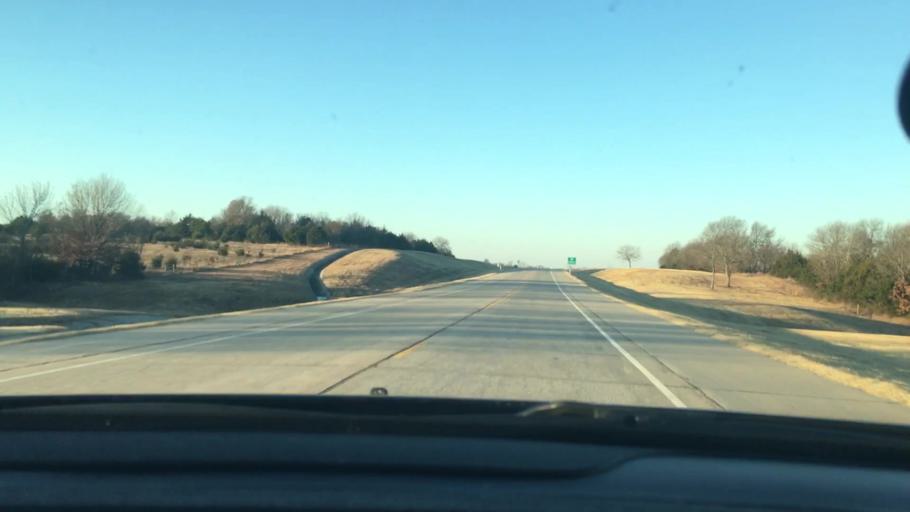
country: US
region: Oklahoma
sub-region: Murray County
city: Sulphur
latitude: 34.5492
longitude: -96.9485
